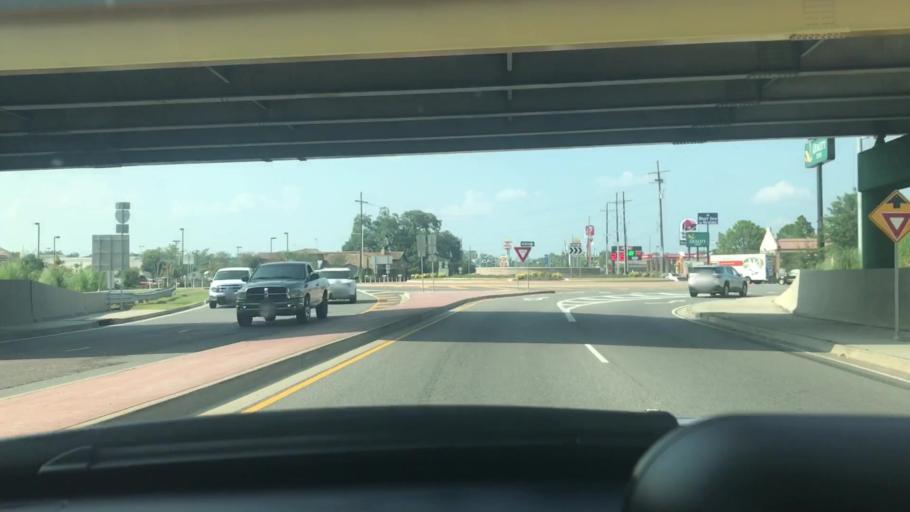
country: US
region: Louisiana
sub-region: Tangipahoa Parish
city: Hammond
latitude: 30.4789
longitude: -90.4571
